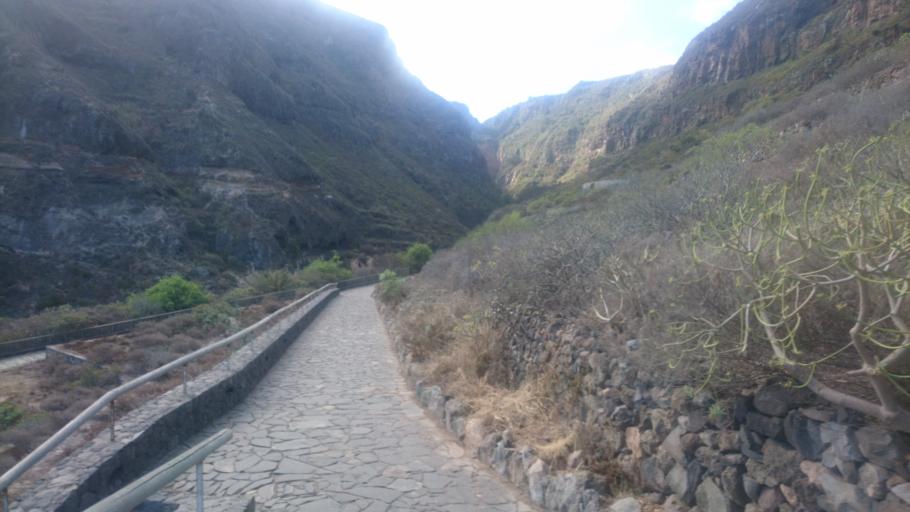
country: ES
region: Canary Islands
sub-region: Provincia de Santa Cruz de Tenerife
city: San Juan de la Rambla
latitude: 28.3913
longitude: -16.6270
